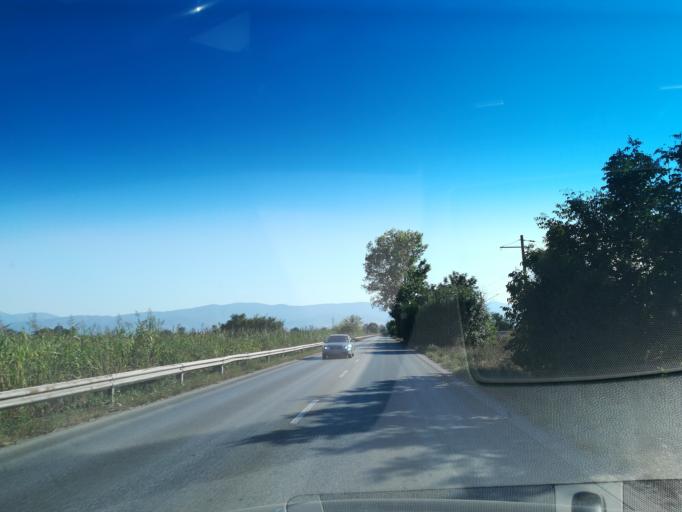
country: BG
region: Plovdiv
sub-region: Obshtina Plovdiv
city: Plovdiv
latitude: 42.1628
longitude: 24.8134
